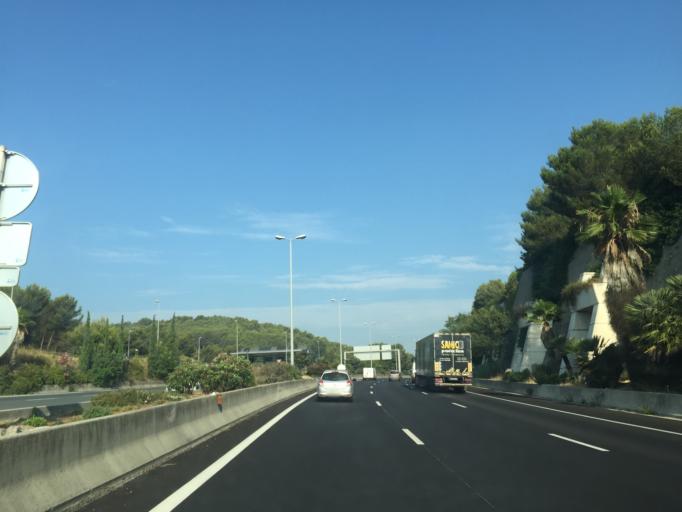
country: FR
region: Provence-Alpes-Cote d'Azur
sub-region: Departement des Alpes-Maritimes
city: Vallauris
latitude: 43.6028
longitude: 7.0752
